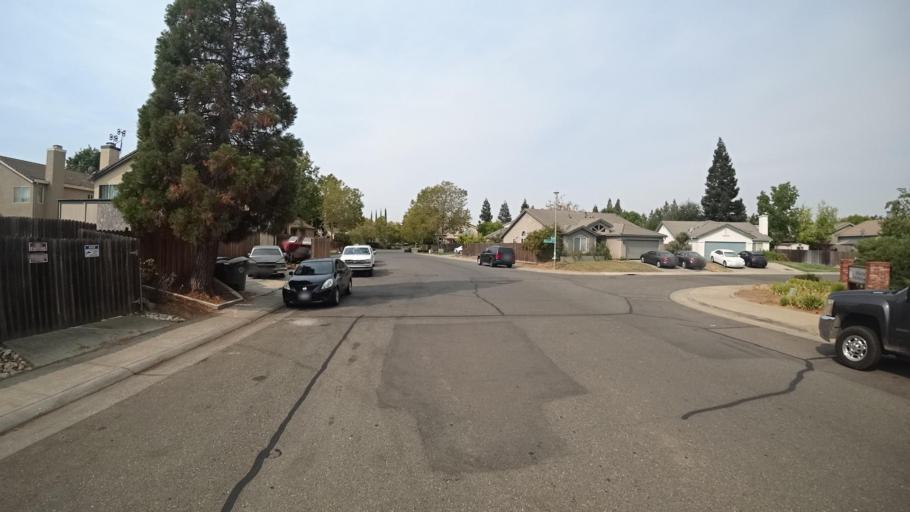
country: US
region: California
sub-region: Sacramento County
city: Laguna
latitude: 38.4152
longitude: -121.4050
